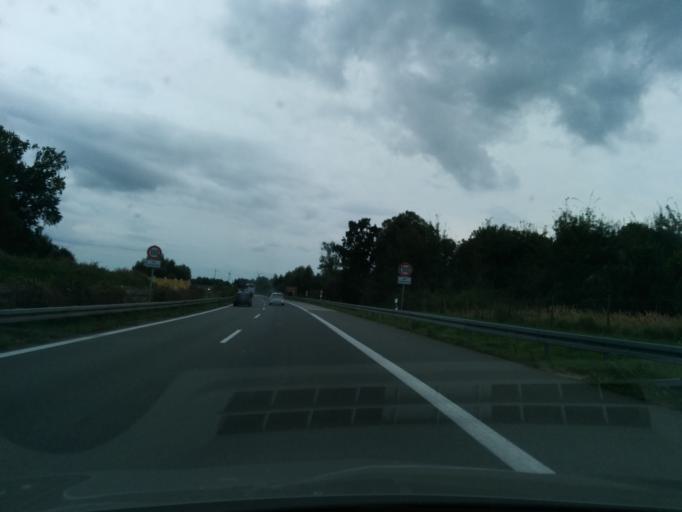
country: DE
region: Mecklenburg-Vorpommern
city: Jarmen
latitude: 53.9333
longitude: 13.3505
